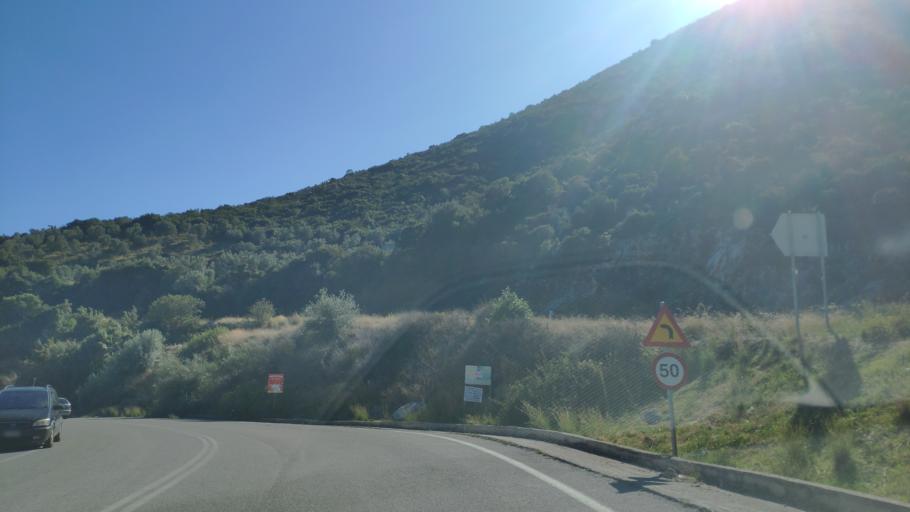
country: GR
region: Peloponnese
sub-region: Nomos Argolidos
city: Palaia Epidavros
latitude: 37.6116
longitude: 23.1521
